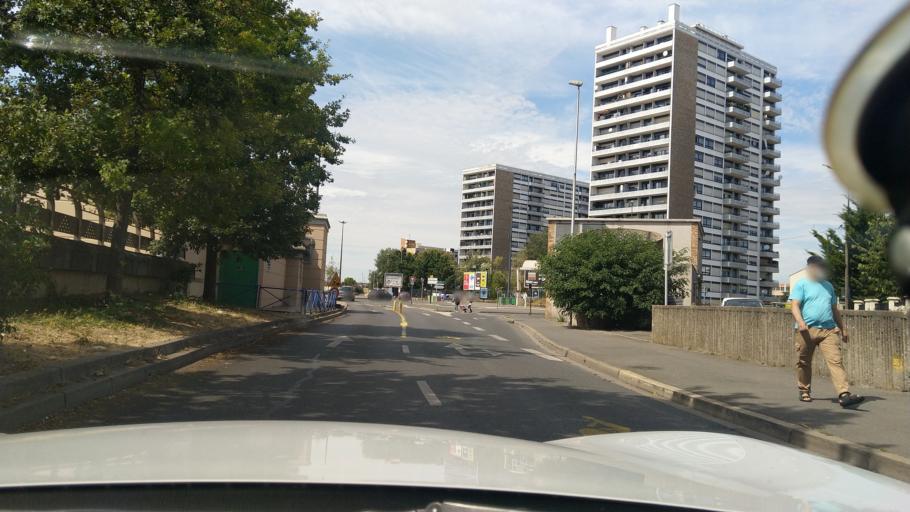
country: FR
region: Ile-de-France
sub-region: Departement de Seine-Saint-Denis
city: Drancy
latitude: 48.9125
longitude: 2.4379
